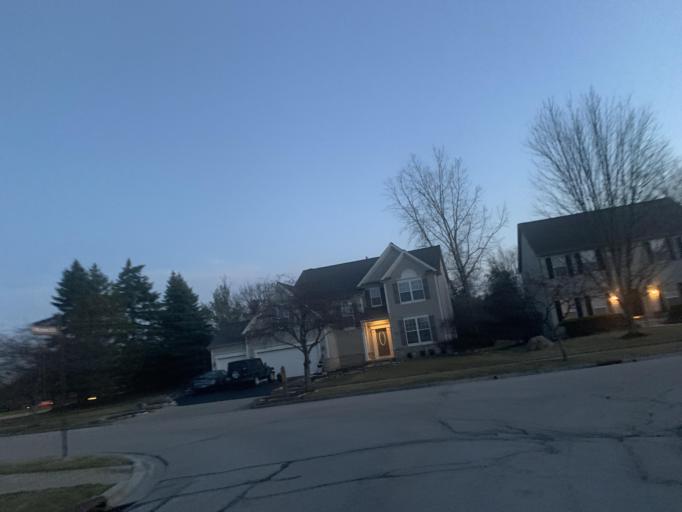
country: US
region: Ohio
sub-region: Franklin County
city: Dublin
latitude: 40.1249
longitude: -83.1523
